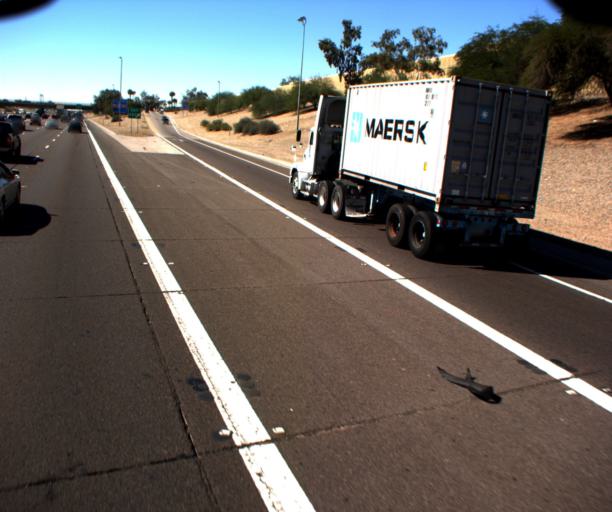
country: US
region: Arizona
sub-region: Maricopa County
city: Tolleson
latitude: 33.4630
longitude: -112.1983
